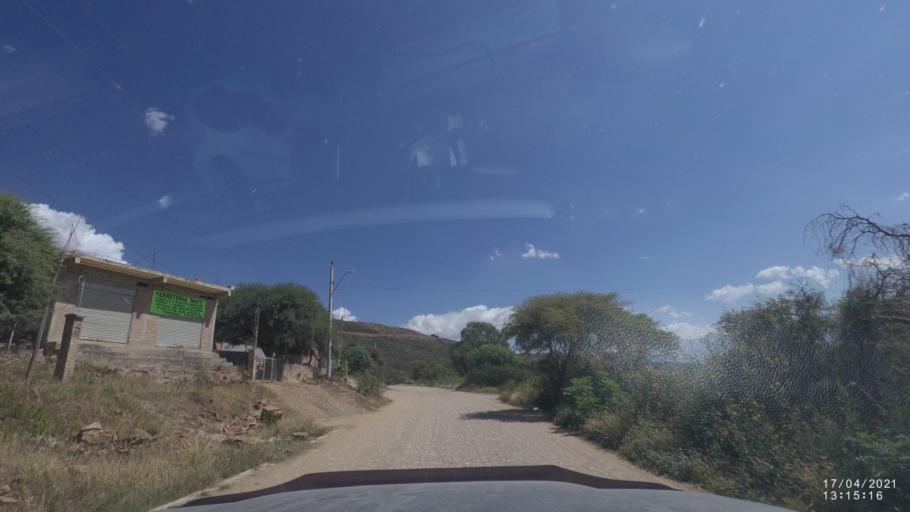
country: BO
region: Cochabamba
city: Cochabamba
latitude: -17.4167
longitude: -66.2303
